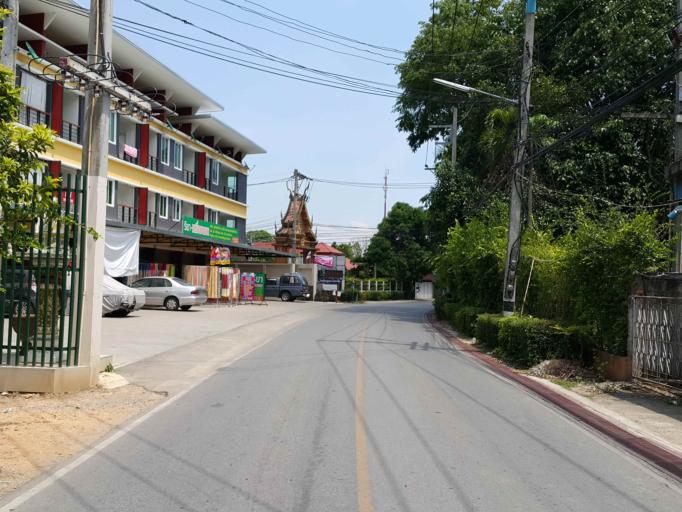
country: TH
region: Chiang Mai
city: Chiang Mai
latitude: 18.8423
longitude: 98.9890
